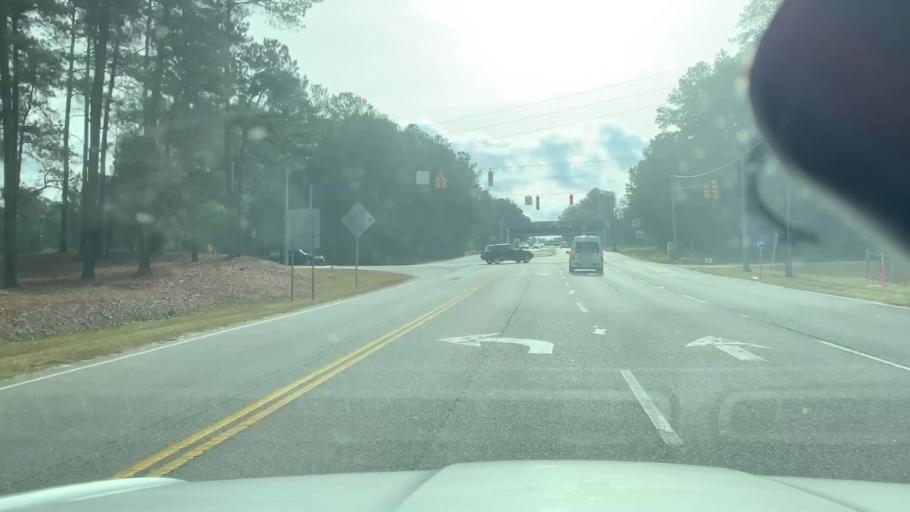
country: US
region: South Carolina
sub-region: Richland County
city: Woodfield
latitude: 34.0725
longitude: -80.9158
